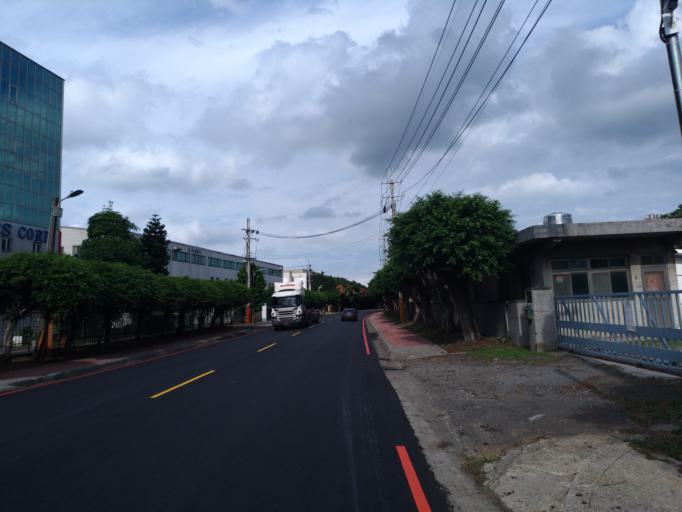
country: TW
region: Taiwan
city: Daxi
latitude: 24.9285
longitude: 121.1707
